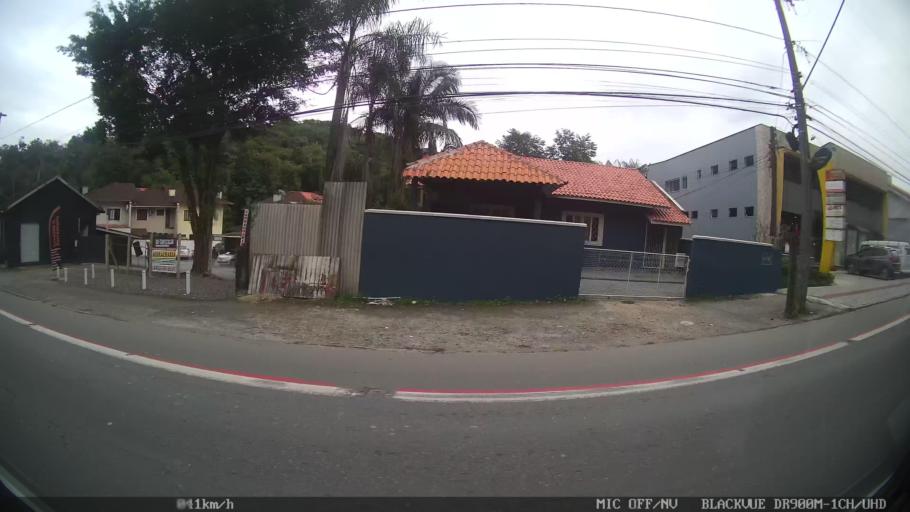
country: BR
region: Santa Catarina
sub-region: Joinville
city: Joinville
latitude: -26.2849
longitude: -48.8660
